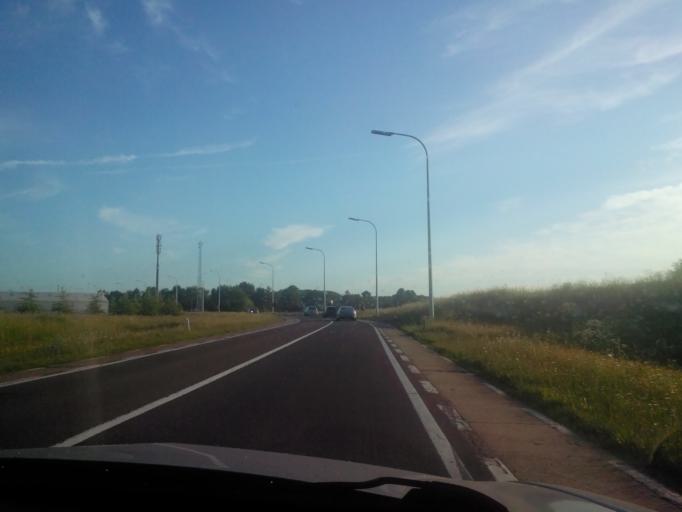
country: BE
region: Flanders
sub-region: Provincie Vlaams-Brabant
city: Bekkevoort
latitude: 50.9622
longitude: 4.9318
